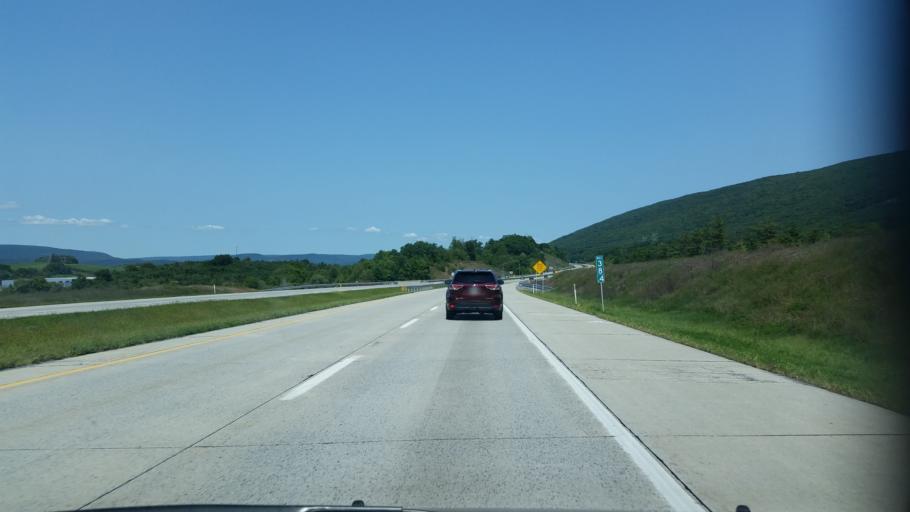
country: US
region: Pennsylvania
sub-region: Blair County
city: Greenwood
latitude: 40.5602
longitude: -78.3294
